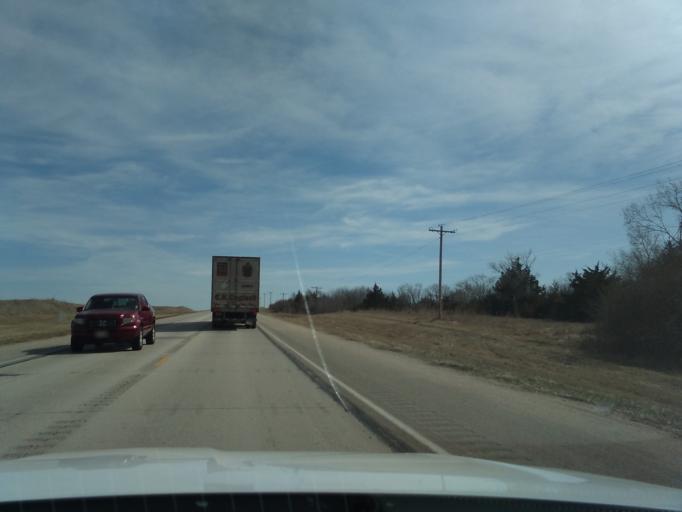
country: US
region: Nebraska
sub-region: Lancaster County
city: Hickman
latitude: 40.6538
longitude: -96.7708
